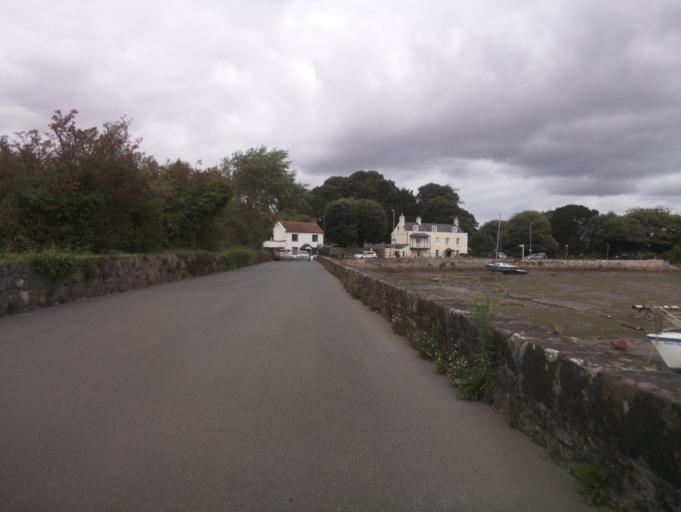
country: GB
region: England
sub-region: Devon
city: Starcross
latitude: 50.6176
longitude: -3.4489
